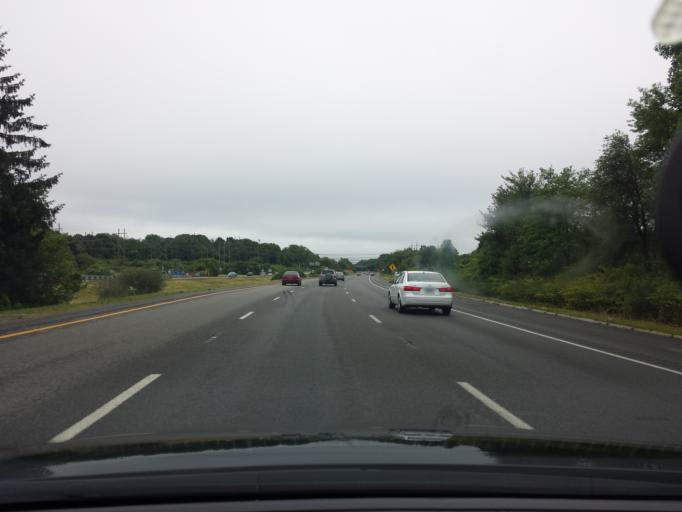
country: US
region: Massachusetts
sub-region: Bristol County
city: Swansea
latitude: 41.7256
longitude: -71.1859
